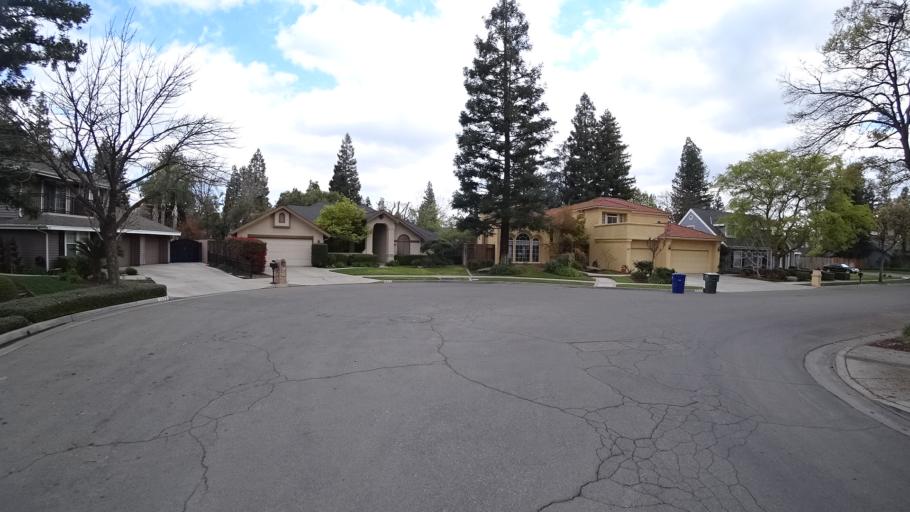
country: US
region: California
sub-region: Fresno County
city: Fresno
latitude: 36.8325
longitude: -119.8146
